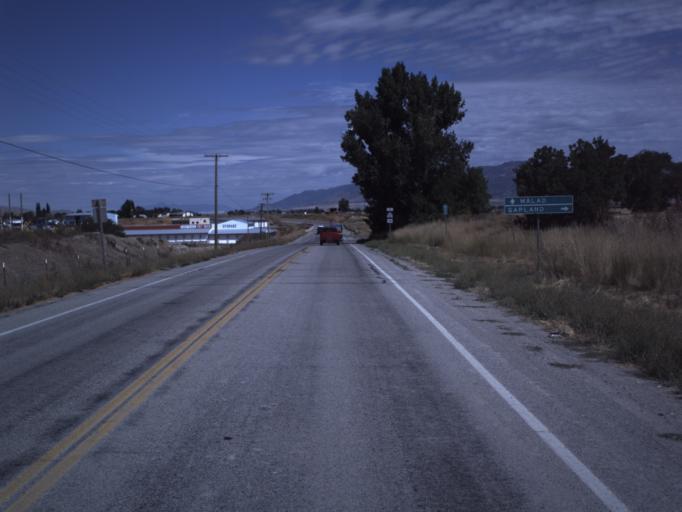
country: US
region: Utah
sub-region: Box Elder County
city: Garland
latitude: 41.7381
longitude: -112.1435
